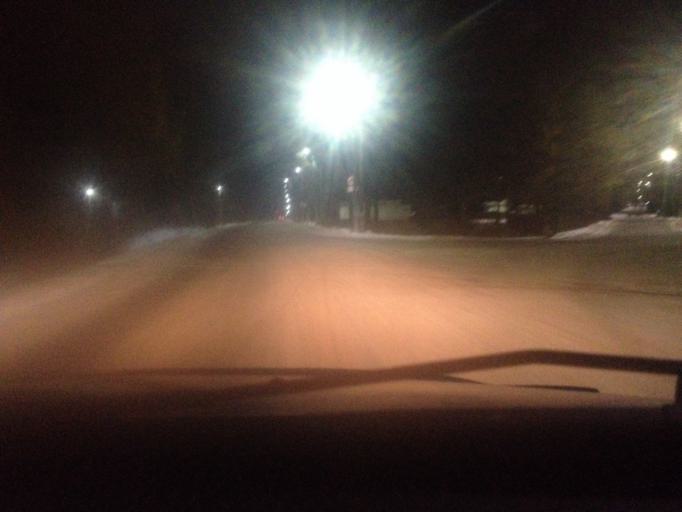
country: RU
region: Tula
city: Leninskiy
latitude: 54.2751
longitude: 37.4502
